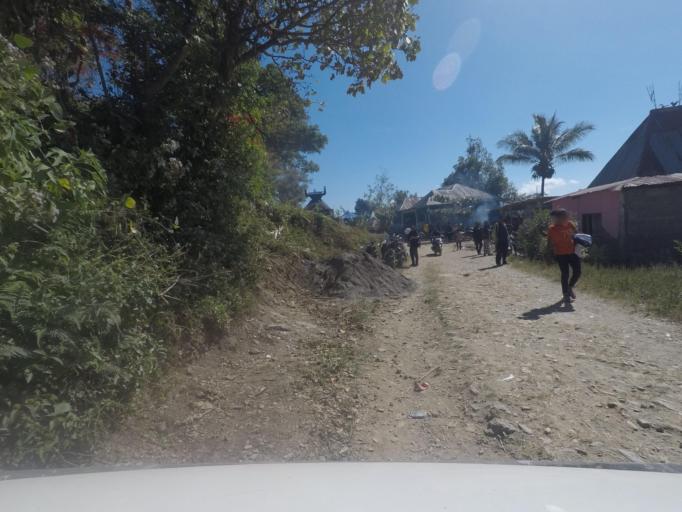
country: TL
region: Ermera
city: Gleno
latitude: -8.7235
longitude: 125.3322
